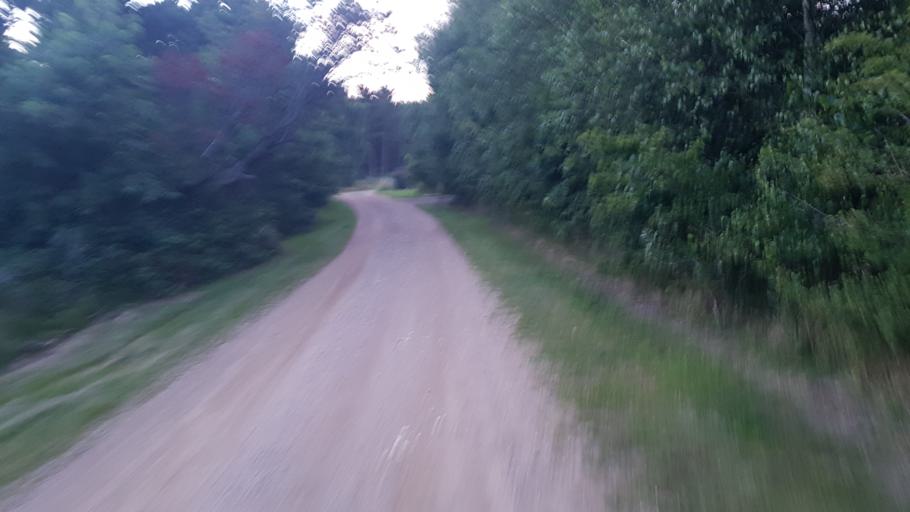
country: DE
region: Schleswig-Holstein
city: List
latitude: 55.0923
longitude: 8.5332
